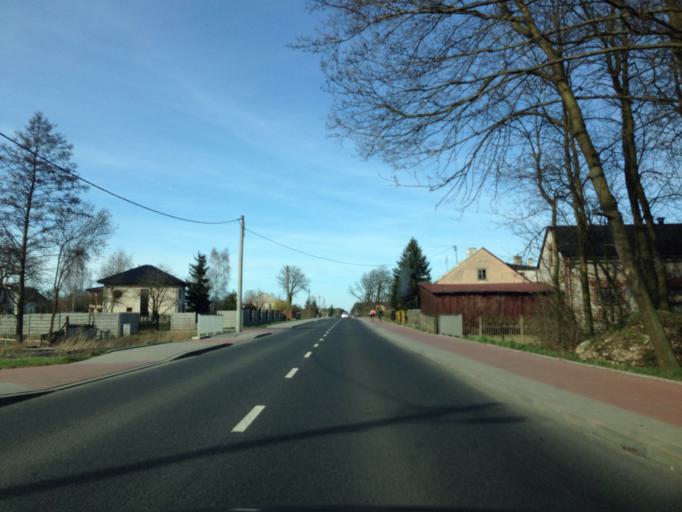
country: PL
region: Lodz Voivodeship
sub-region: Powiat poddebicki
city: Wartkowice
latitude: 51.9437
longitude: 18.9978
